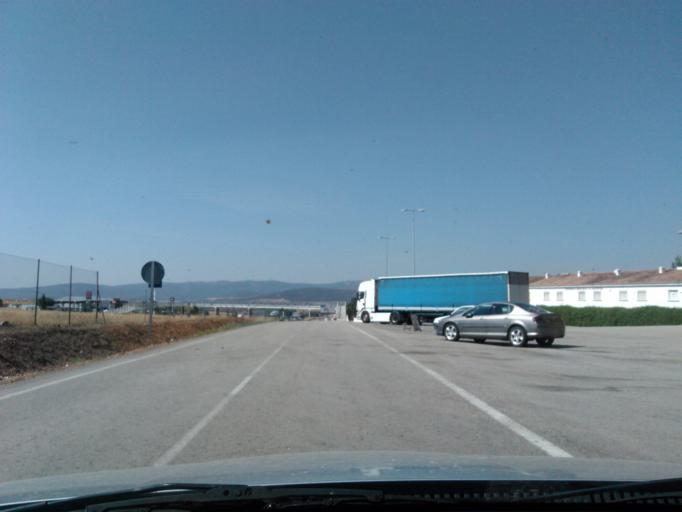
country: ES
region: Castille-La Mancha
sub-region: Provincia de Ciudad Real
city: Viso del Marques
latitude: 38.5097
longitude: -3.4959
